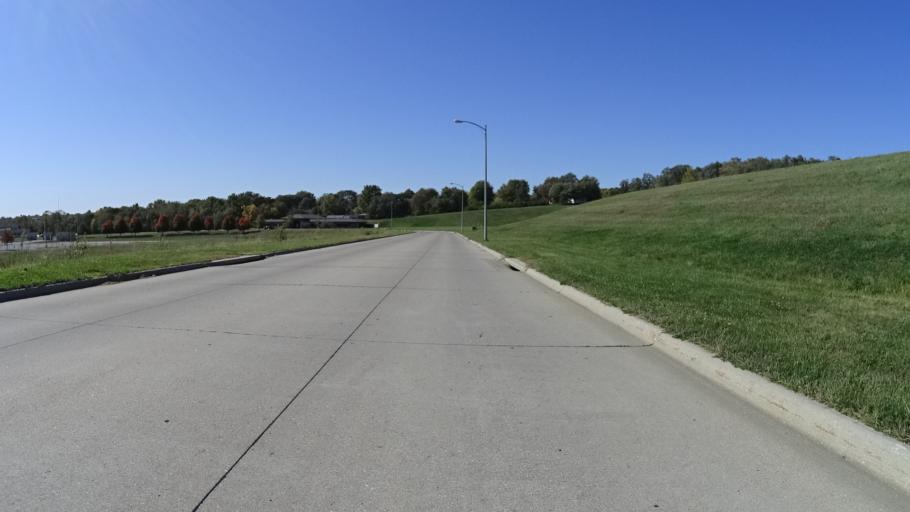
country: US
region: Nebraska
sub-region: Sarpy County
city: Papillion
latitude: 41.1595
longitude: -96.0293
